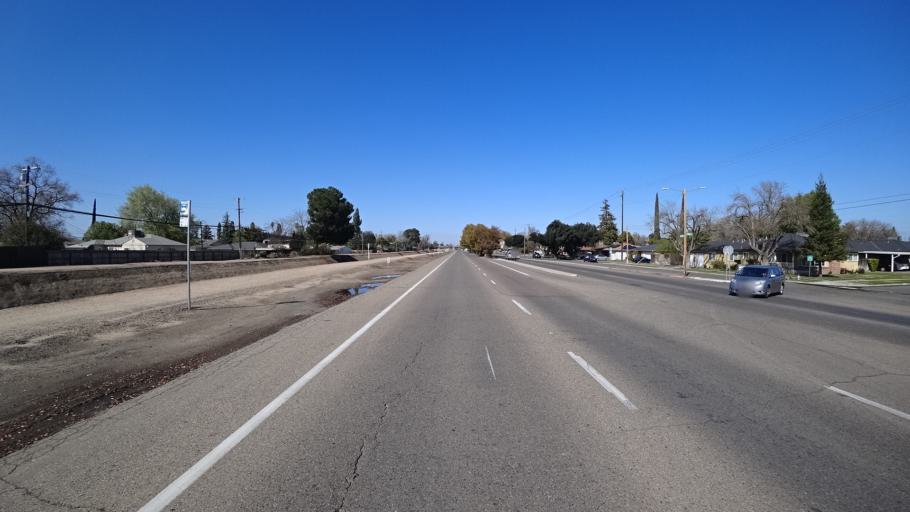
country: US
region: California
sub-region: Fresno County
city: Fresno
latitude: 36.7796
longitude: -119.7764
